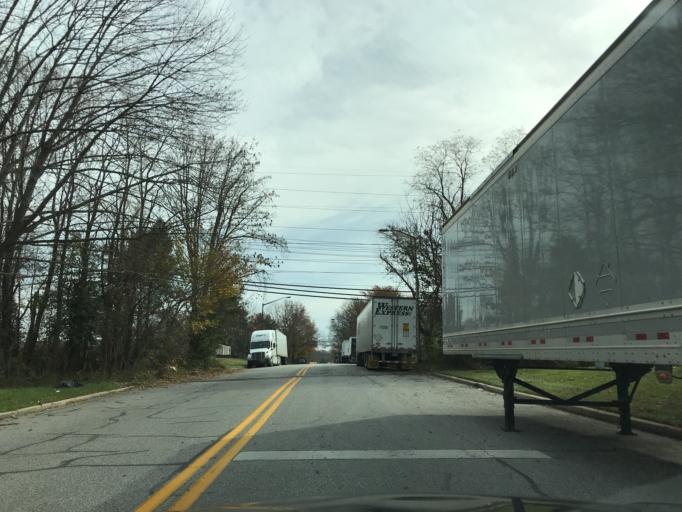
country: US
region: Maryland
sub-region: Howard County
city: Riverside
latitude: 39.1748
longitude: -76.8452
